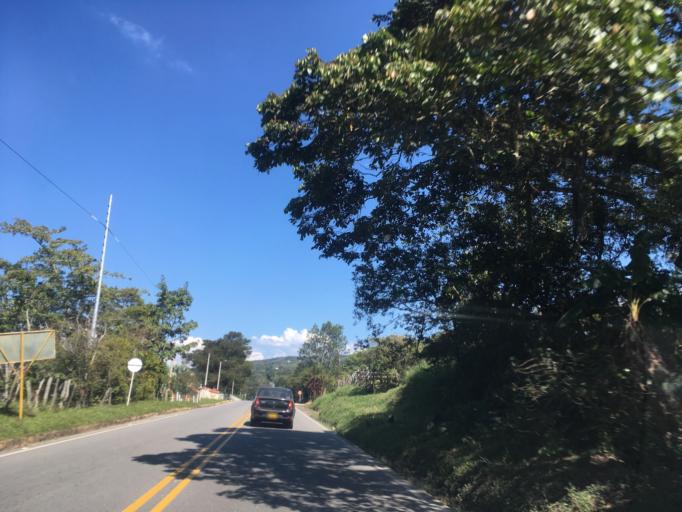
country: CO
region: Santander
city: Suaita
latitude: 6.0762
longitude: -73.4026
